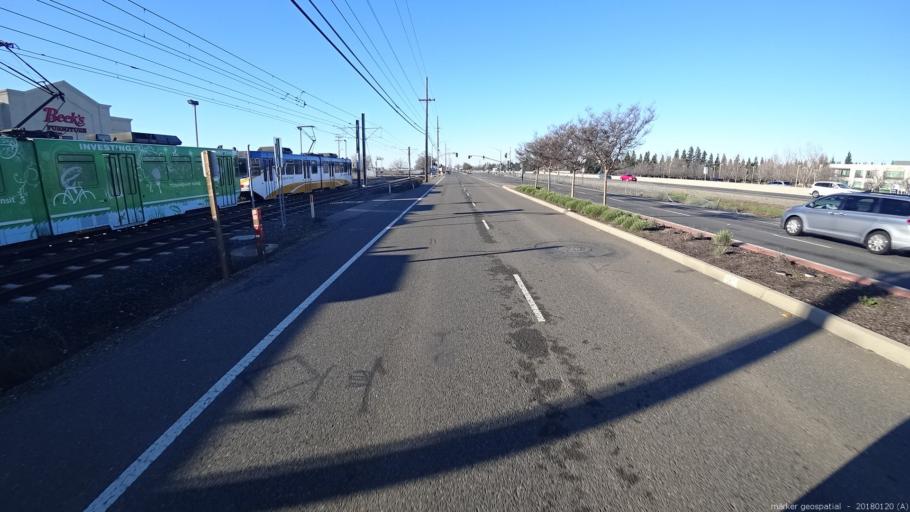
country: US
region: California
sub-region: Sacramento County
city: Gold River
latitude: 38.6243
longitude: -121.2286
